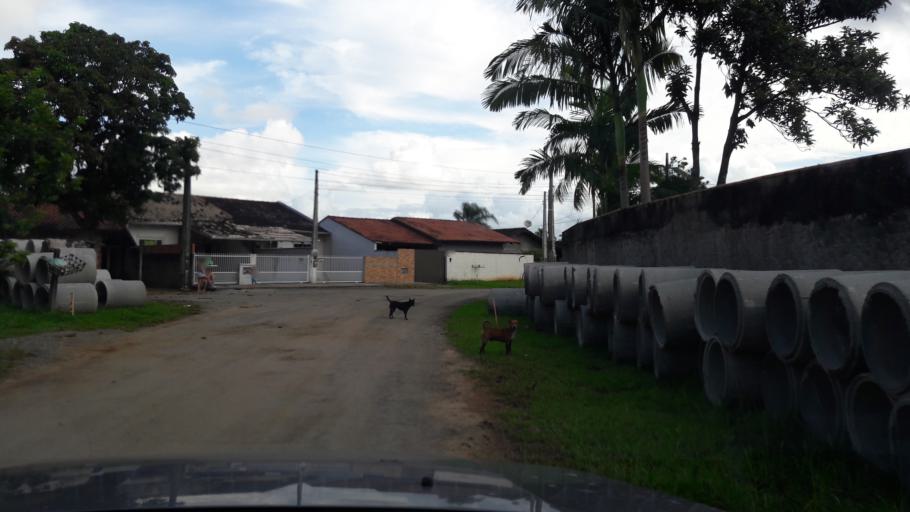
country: BR
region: Santa Catarina
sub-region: Joinville
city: Joinville
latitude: -26.3226
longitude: -48.8203
